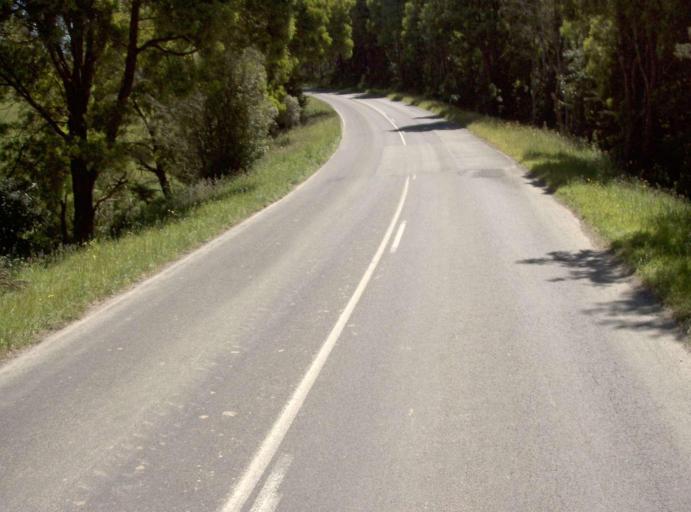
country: AU
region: Victoria
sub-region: Latrobe
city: Morwell
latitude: -38.6899
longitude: 146.1354
